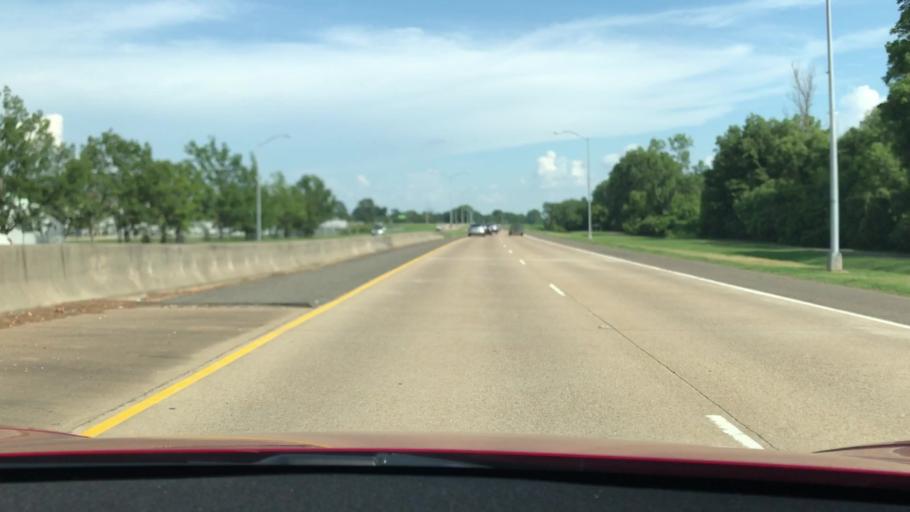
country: US
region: Louisiana
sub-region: Bossier Parish
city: Bossier City
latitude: 32.4829
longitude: -93.6853
